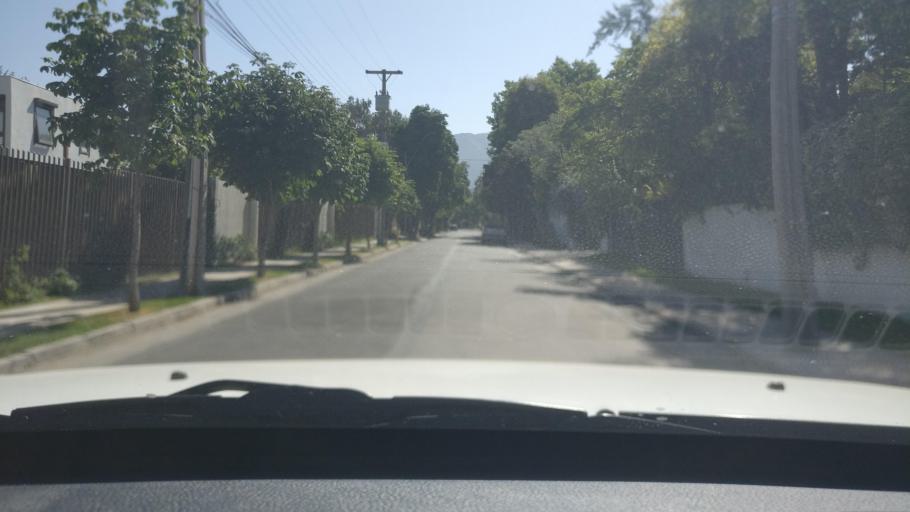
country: CL
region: Santiago Metropolitan
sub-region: Provincia de Santiago
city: Villa Presidente Frei, Nunoa, Santiago, Chile
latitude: -33.3759
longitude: -70.5152
